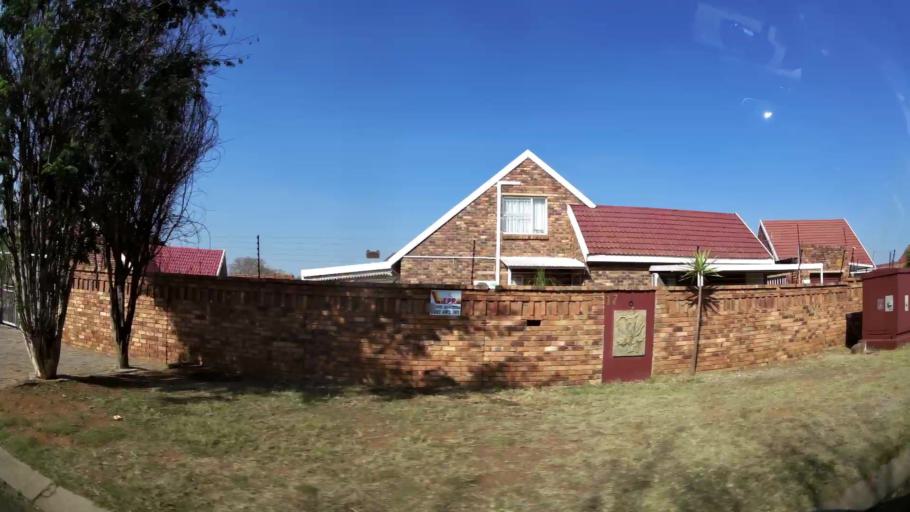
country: ZA
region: Gauteng
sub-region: West Rand District Municipality
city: Randfontein
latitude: -26.1781
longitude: 27.6844
